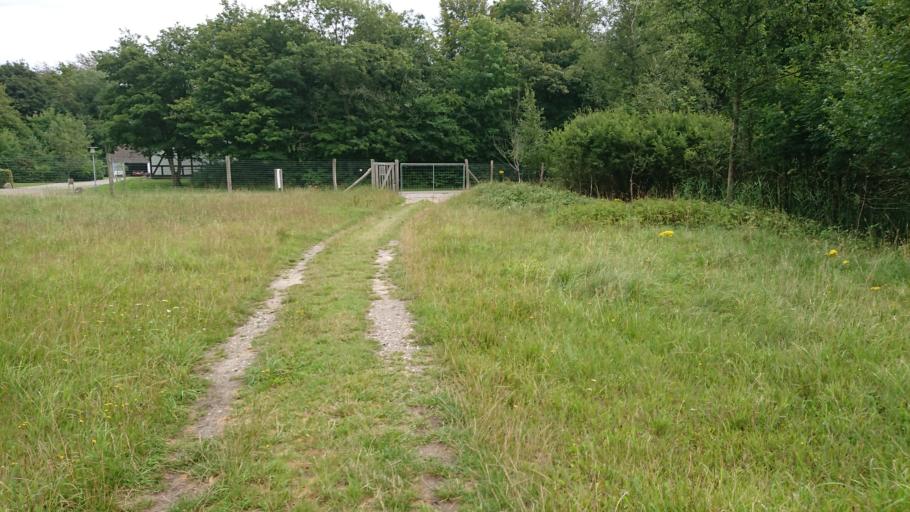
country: DK
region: North Denmark
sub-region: Hjorring Kommune
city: Sindal
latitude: 57.4828
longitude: 10.1774
